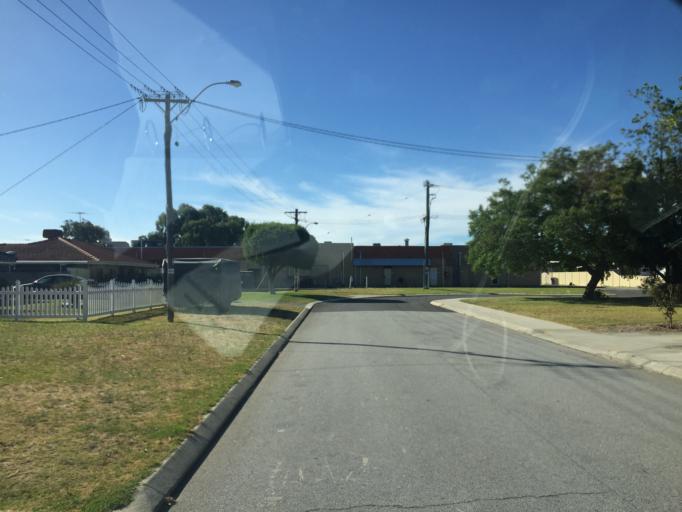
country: AU
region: Western Australia
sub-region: Canning
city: East Cannington
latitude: -32.0145
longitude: 115.9663
